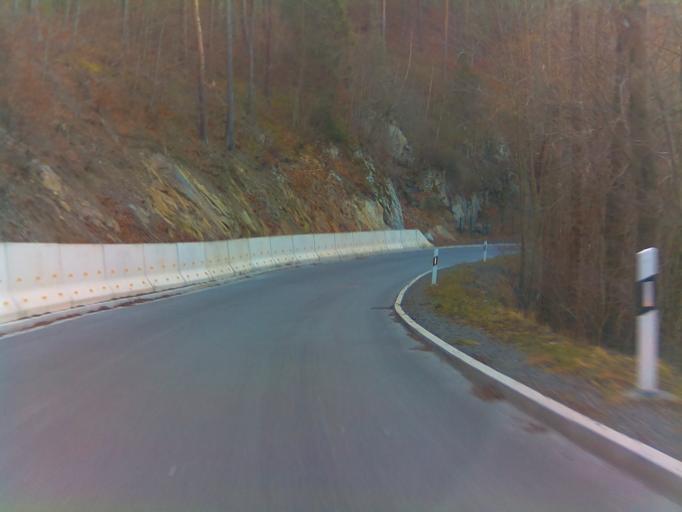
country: DE
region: Thuringia
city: Grafenthal
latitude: 50.5300
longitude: 11.3038
